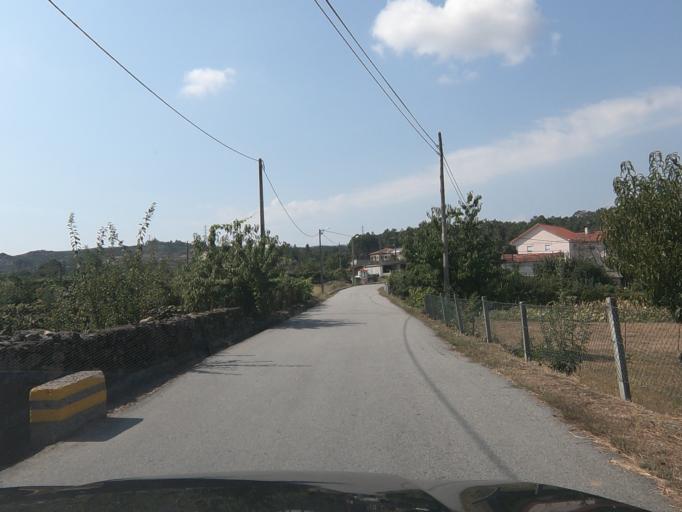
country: PT
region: Vila Real
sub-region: Sabrosa
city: Sabrosa
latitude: 41.3337
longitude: -7.6038
